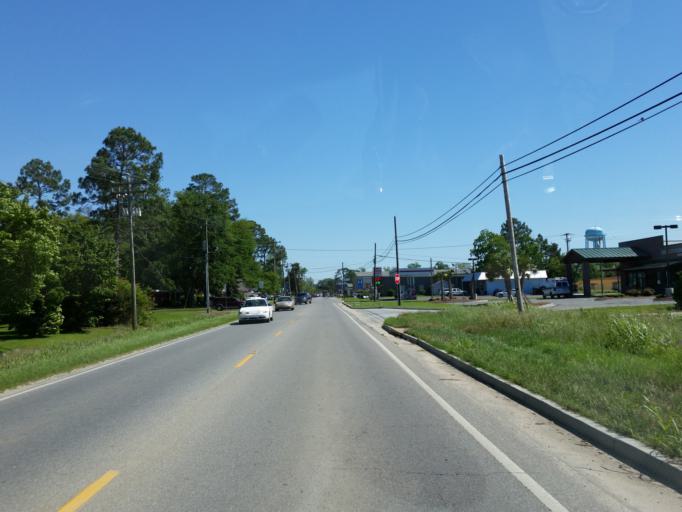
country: US
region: Georgia
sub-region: Cook County
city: Adel
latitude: 31.1447
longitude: -83.4262
